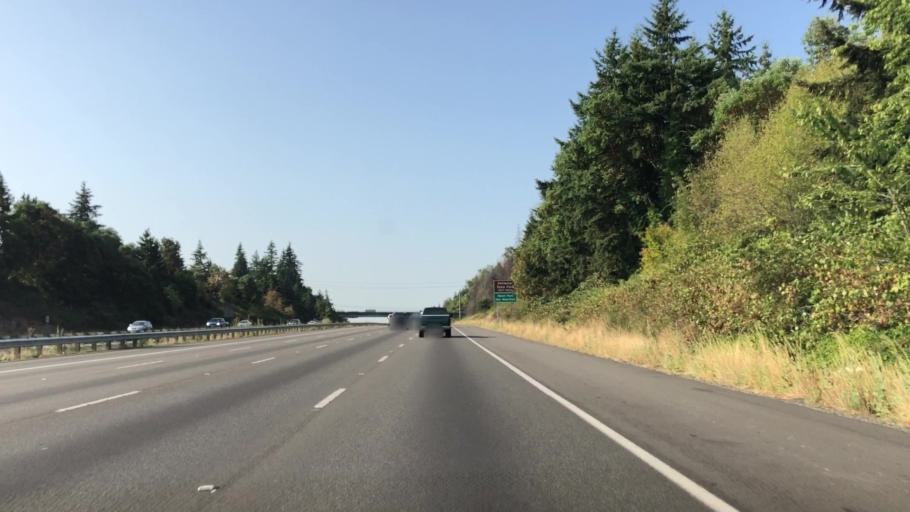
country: US
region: Washington
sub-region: King County
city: Des Moines
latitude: 47.4119
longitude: -122.2913
